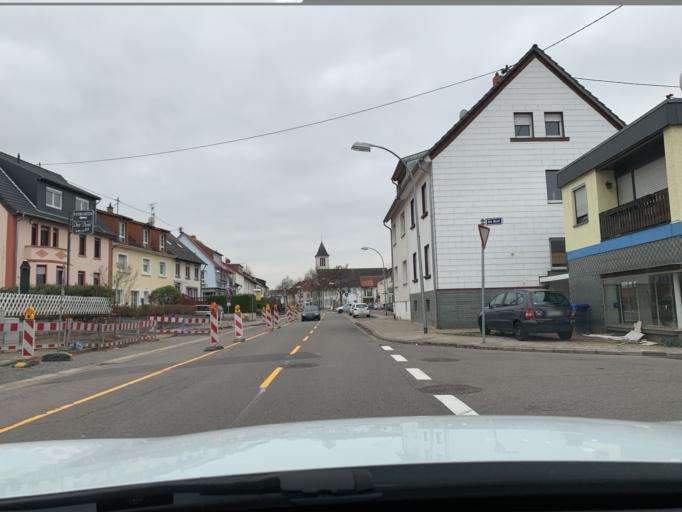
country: DE
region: Saarland
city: Kleinblittersdorf
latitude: 49.1799
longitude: 7.0374
